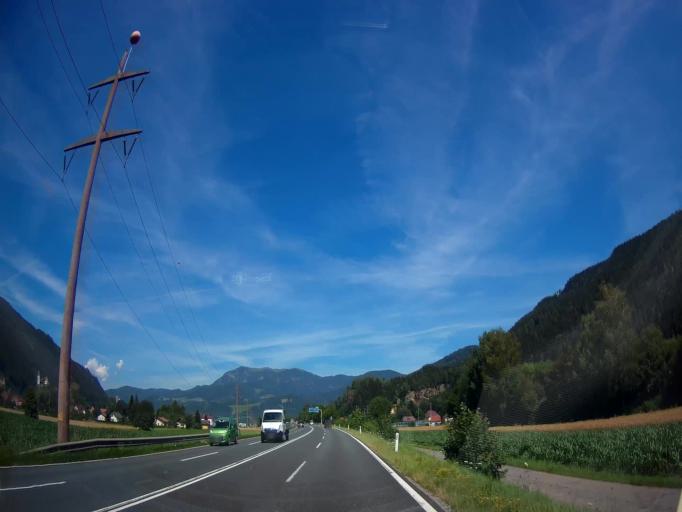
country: AT
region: Carinthia
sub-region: Politischer Bezirk Sankt Veit an der Glan
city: Friesach
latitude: 46.9484
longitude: 14.4210
